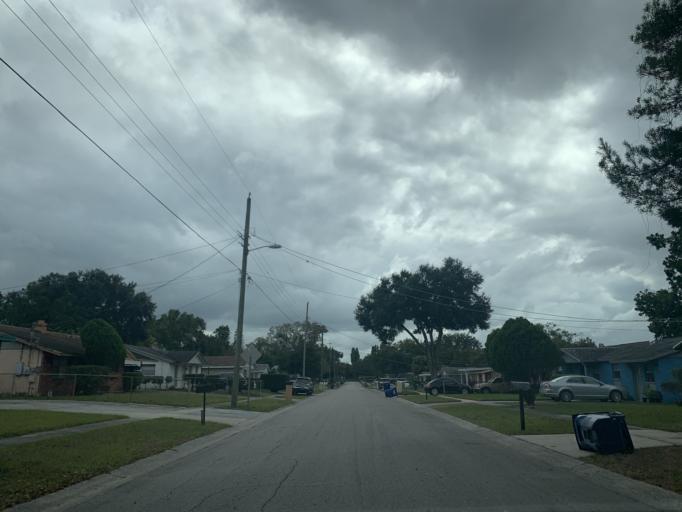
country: US
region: Florida
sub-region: Hillsborough County
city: East Lake-Orient Park
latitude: 27.9882
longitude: -82.4022
